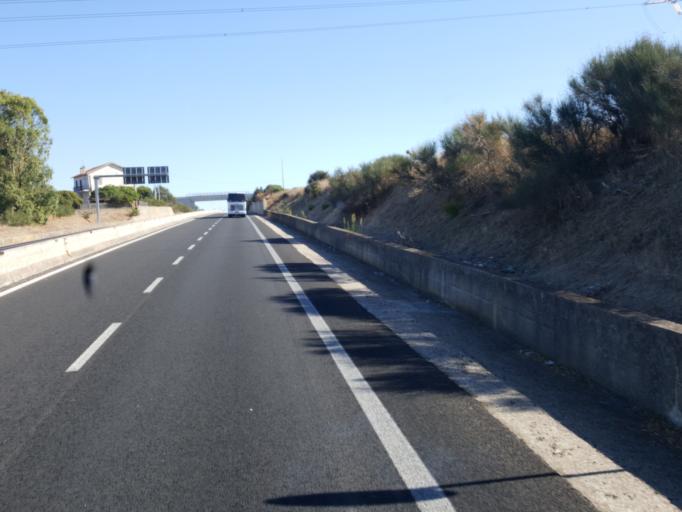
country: IT
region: Latium
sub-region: Citta metropolitana di Roma Capitale
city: Aurelia
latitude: 42.1313
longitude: 11.7934
